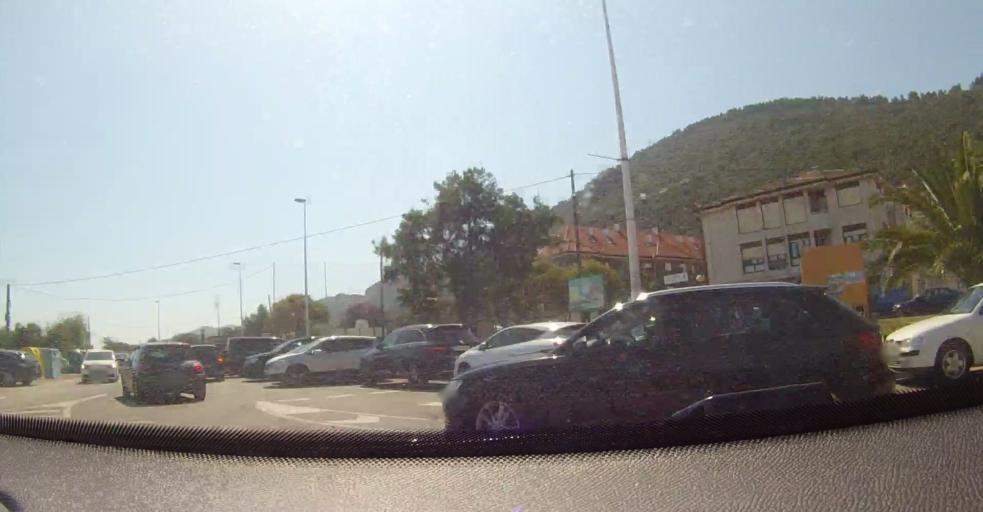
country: ES
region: Cantabria
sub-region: Provincia de Cantabria
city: Argonos
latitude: 43.4723
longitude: -3.5058
